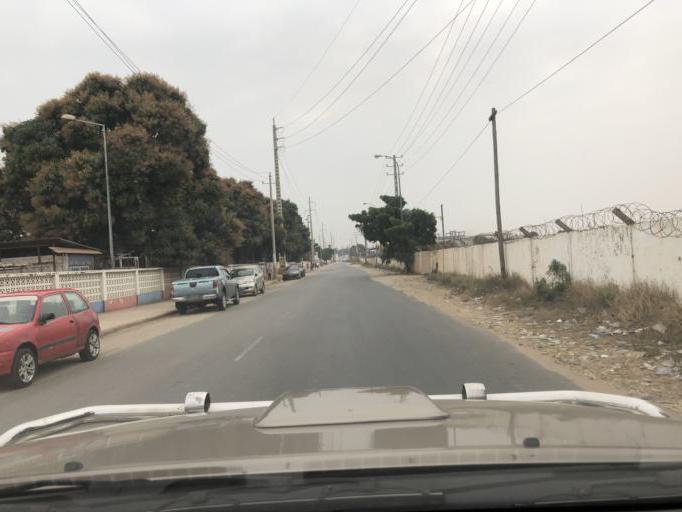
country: AO
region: Luanda
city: Luanda
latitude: -8.8922
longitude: 13.1887
